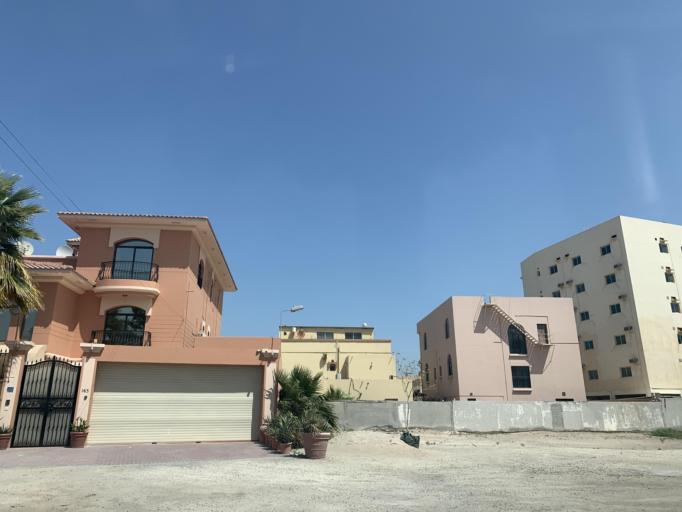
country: BH
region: Manama
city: Manama
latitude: 26.2123
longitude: 50.5705
